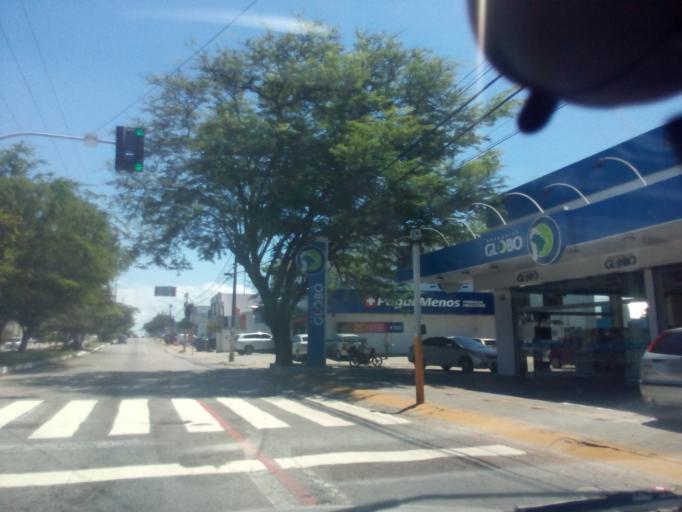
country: BR
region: Rio Grande do Norte
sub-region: Natal
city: Natal
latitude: -5.8373
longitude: -35.2196
